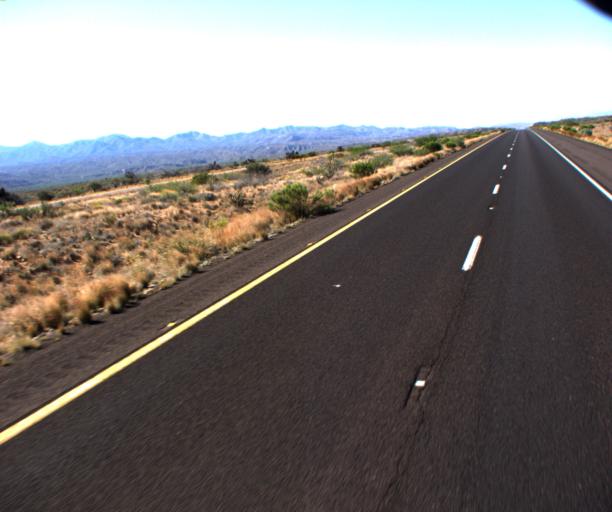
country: US
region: Arizona
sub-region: Mohave County
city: Kingman
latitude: 35.1135
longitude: -113.6668
